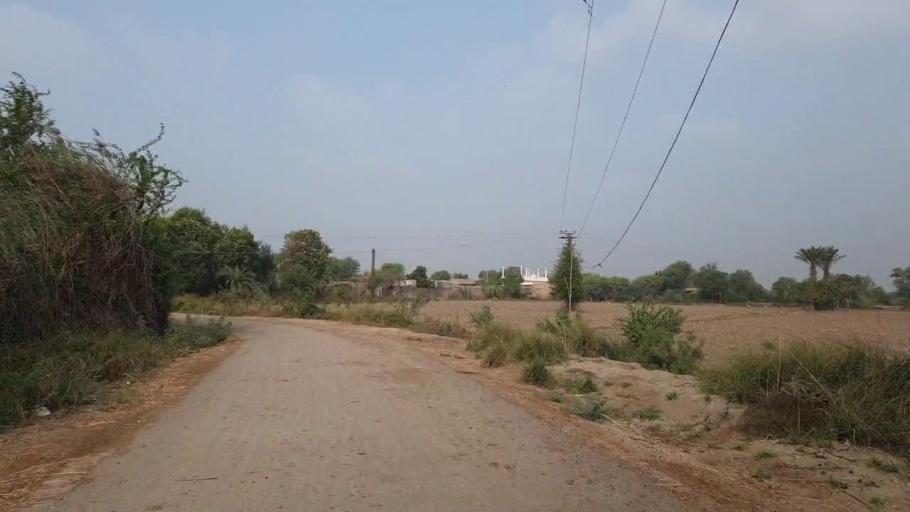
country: PK
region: Sindh
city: Tando Muhammad Khan
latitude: 25.1299
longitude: 68.5955
